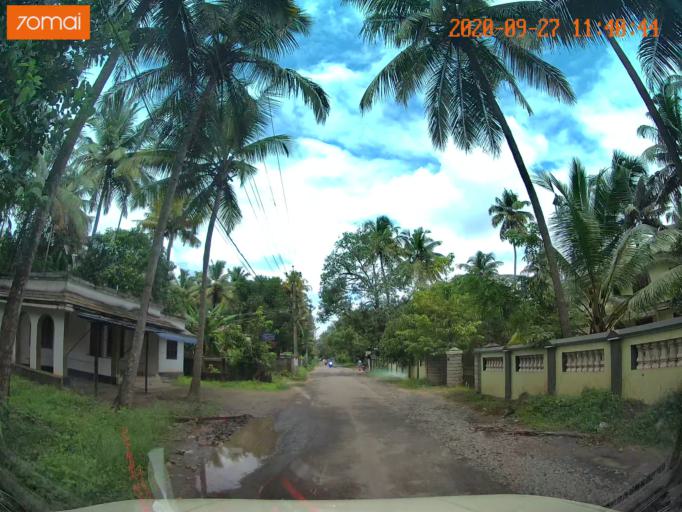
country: IN
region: Kerala
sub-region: Thrissur District
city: Thanniyam
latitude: 10.4699
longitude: 76.1164
